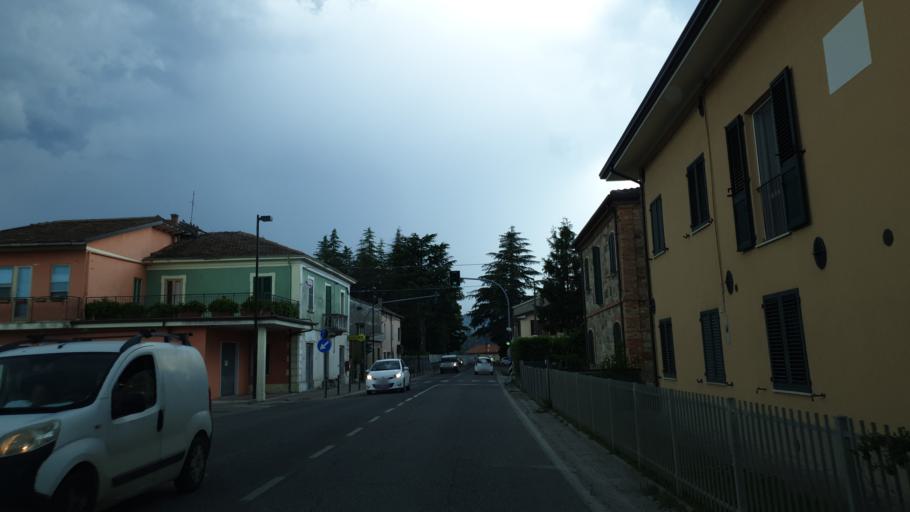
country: IT
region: Emilia-Romagna
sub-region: Provincia di Rimini
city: Secchiano
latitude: 43.9243
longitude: 12.3175
